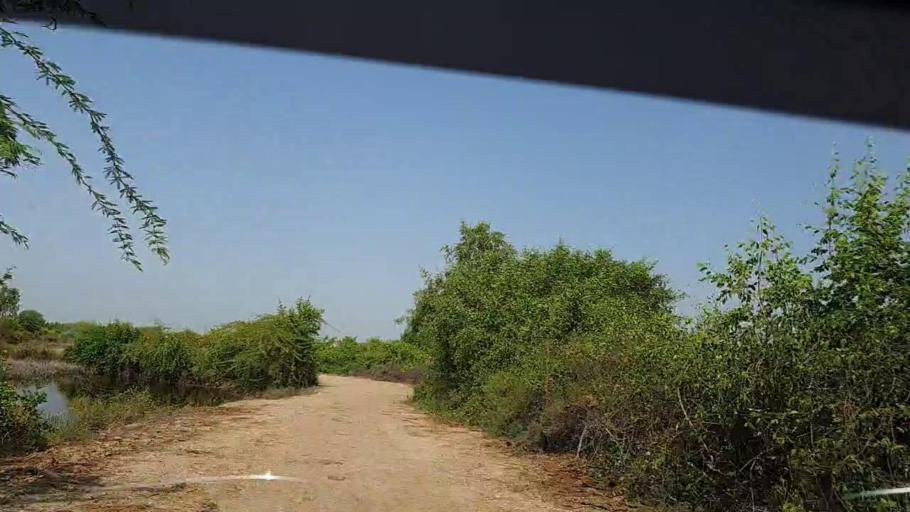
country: PK
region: Sindh
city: Rajo Khanani
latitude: 24.9352
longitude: 68.8800
